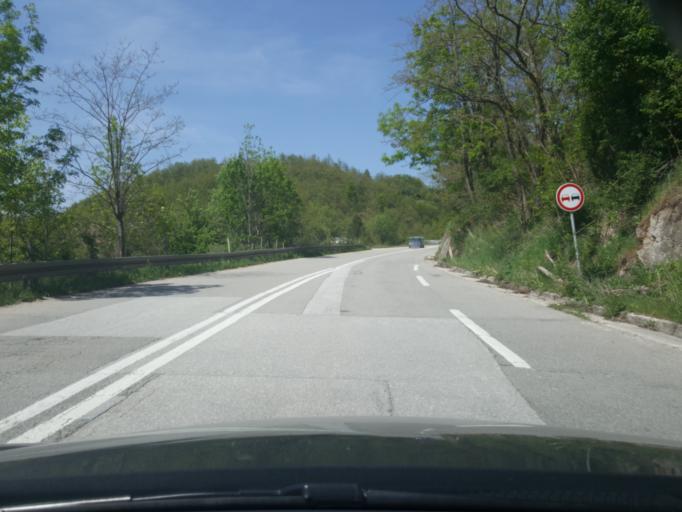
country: RS
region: Central Serbia
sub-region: Zlatiborski Okrug
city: Cajetina
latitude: 43.8066
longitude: 19.6466
